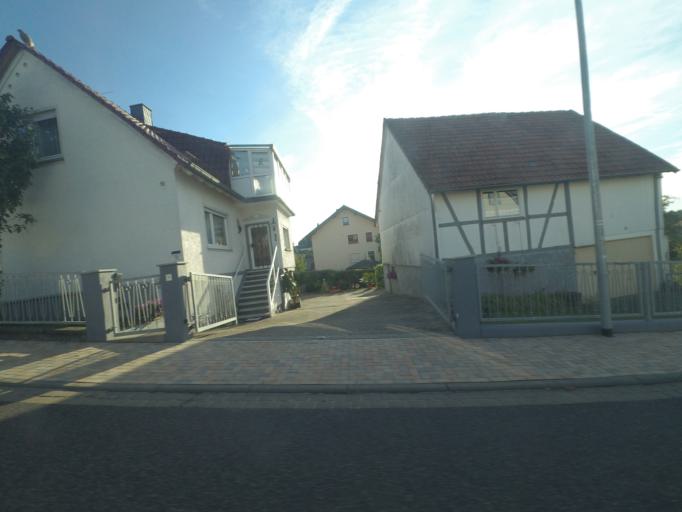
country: DE
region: Hesse
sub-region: Regierungsbezirk Darmstadt
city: Birstein
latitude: 50.3151
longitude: 9.3358
